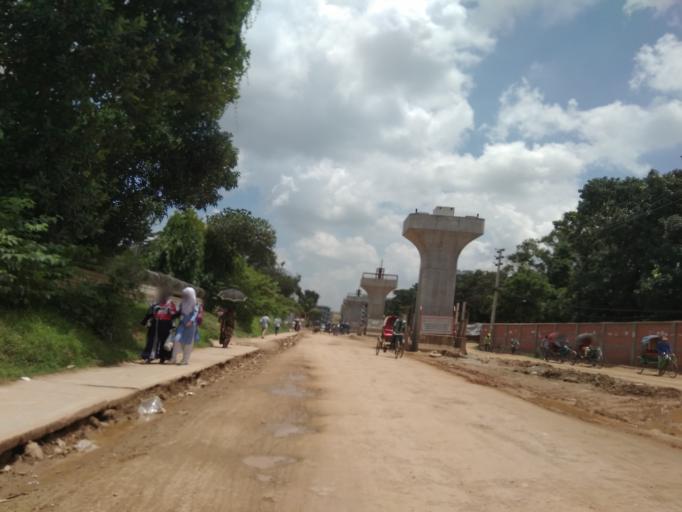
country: BD
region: Dhaka
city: Tungi
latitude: 23.8313
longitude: 90.3637
